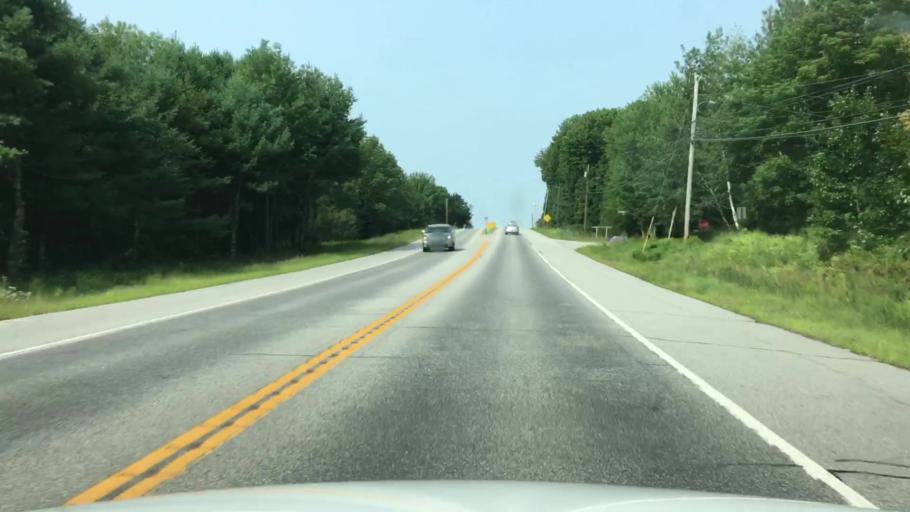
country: US
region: Maine
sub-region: Kennebec County
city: Manchester
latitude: 44.3205
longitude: -69.9148
